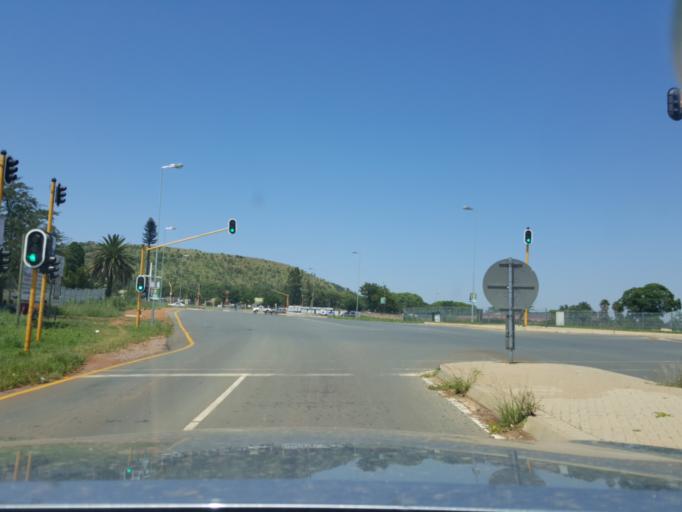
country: ZA
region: Gauteng
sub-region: City of Tshwane Metropolitan Municipality
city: Pretoria
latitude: -25.6823
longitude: 28.2989
